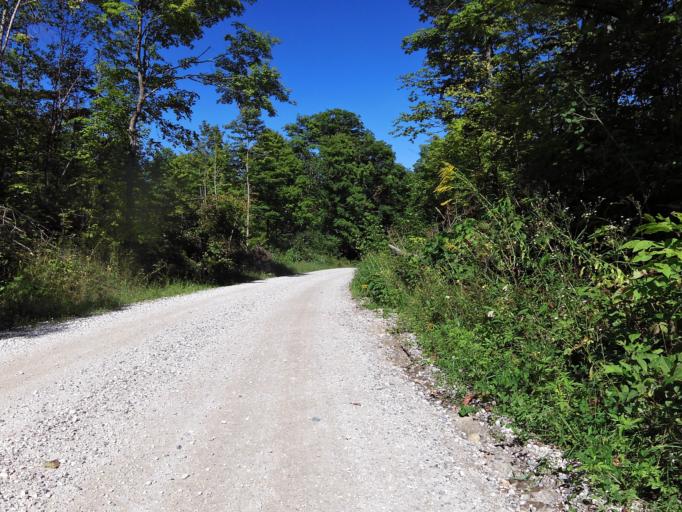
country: CA
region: Ontario
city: Renfrew
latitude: 45.1336
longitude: -76.7112
